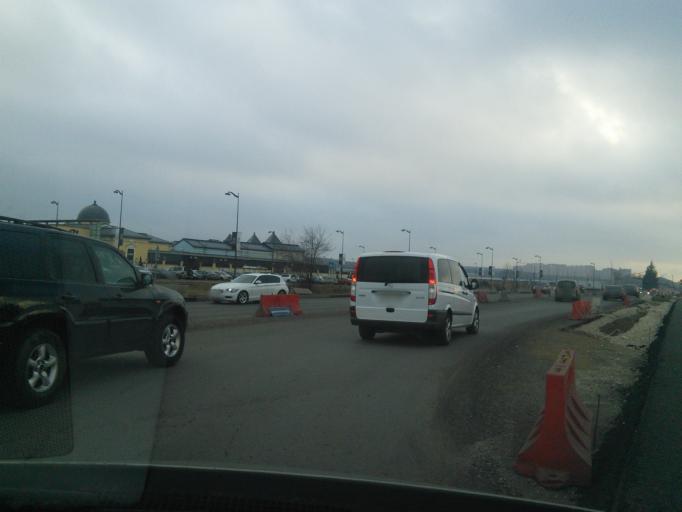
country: RU
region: Moskovskaya
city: Lyubertsy
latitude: 55.6627
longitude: 37.8775
